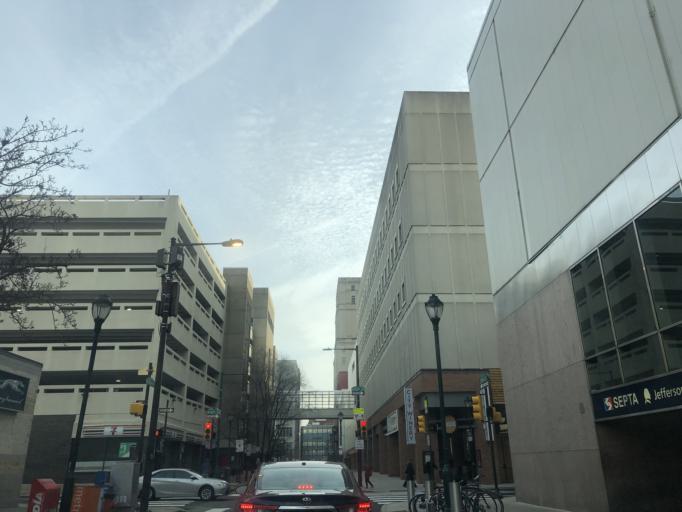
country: US
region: Pennsylvania
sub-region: Philadelphia County
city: Philadelphia
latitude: 39.9526
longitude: -75.1569
